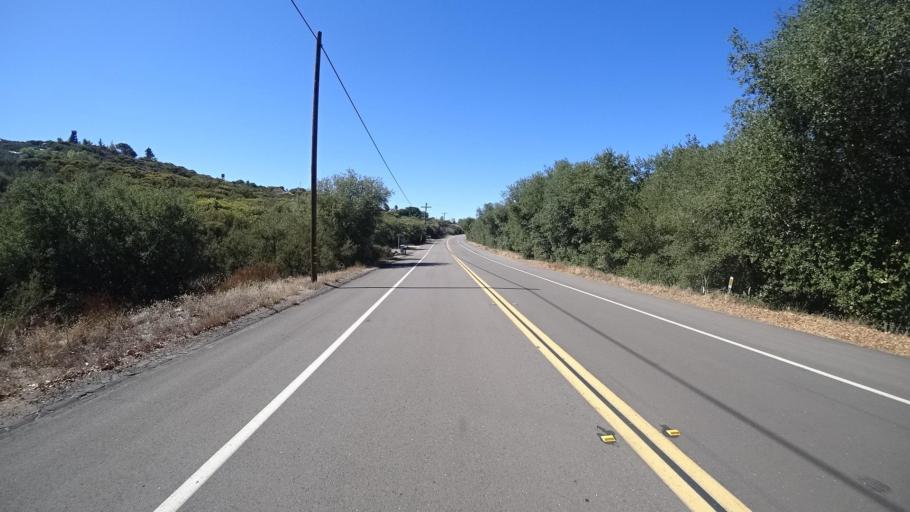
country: US
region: California
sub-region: San Diego County
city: Alpine
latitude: 32.7645
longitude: -116.6818
